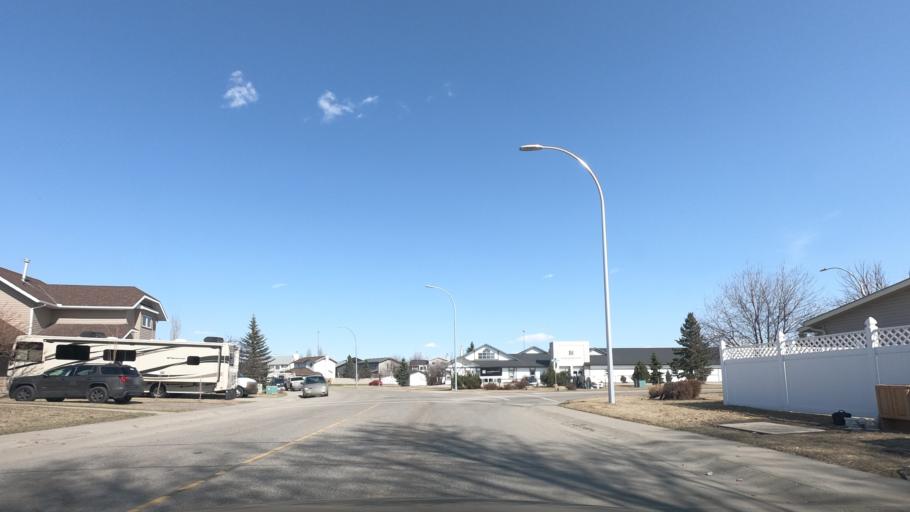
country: CA
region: Alberta
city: Airdrie
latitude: 51.2794
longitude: -114.0065
